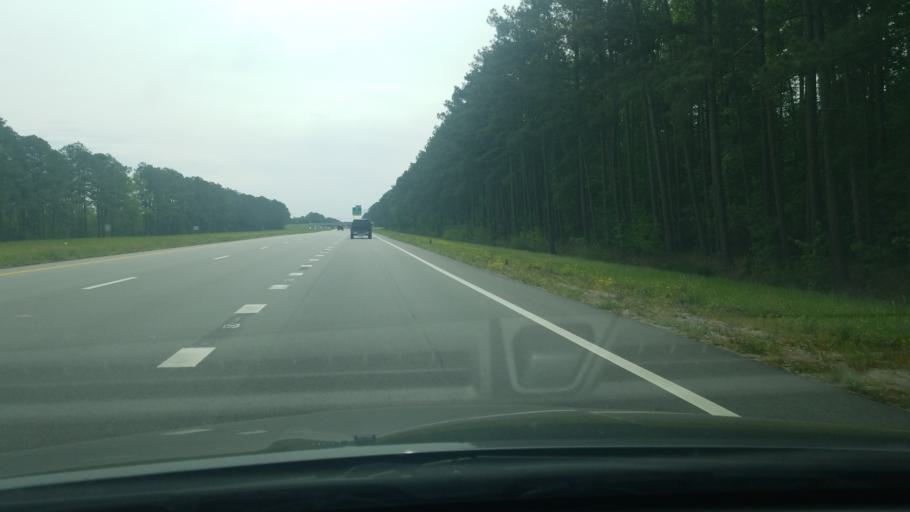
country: US
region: North Carolina
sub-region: Craven County
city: River Bend
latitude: 35.1301
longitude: -77.1448
